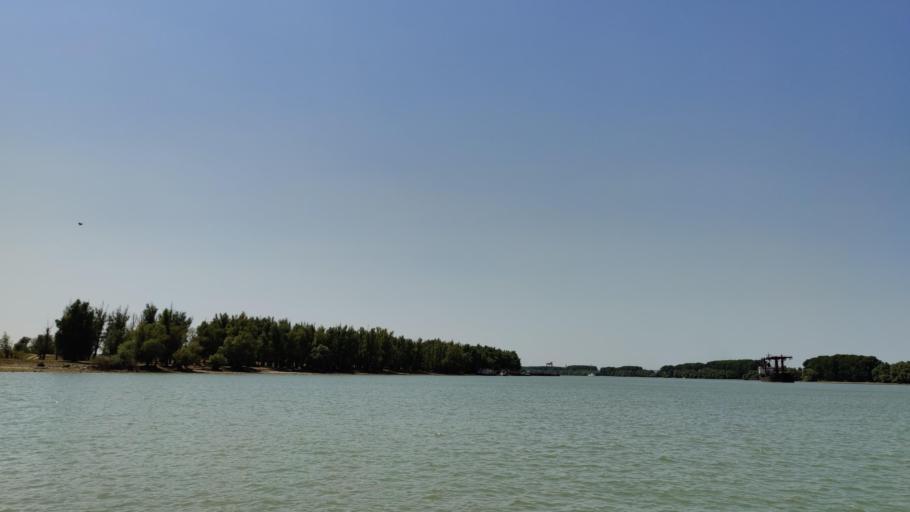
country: RO
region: Tulcea
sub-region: Municipiul Tulcea
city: Tulcea
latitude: 45.2026
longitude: 28.8453
